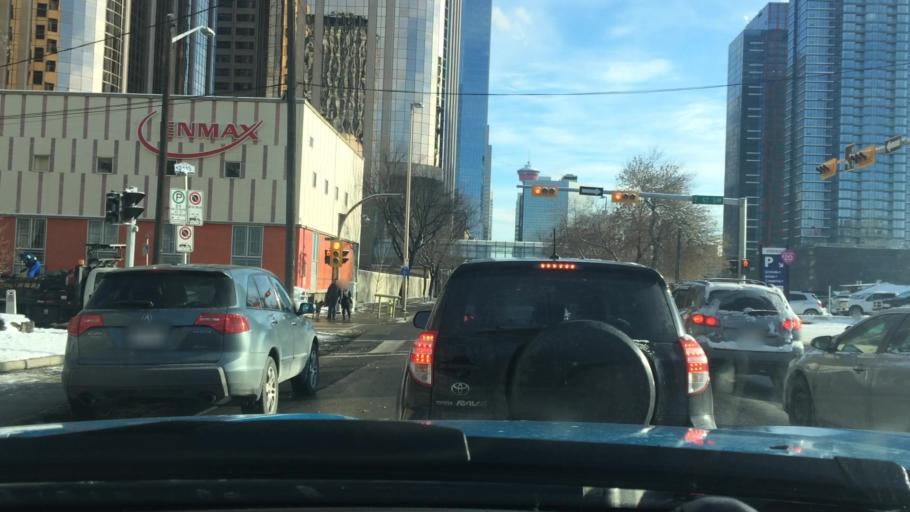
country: CA
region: Alberta
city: Calgary
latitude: 51.0451
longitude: -114.0793
